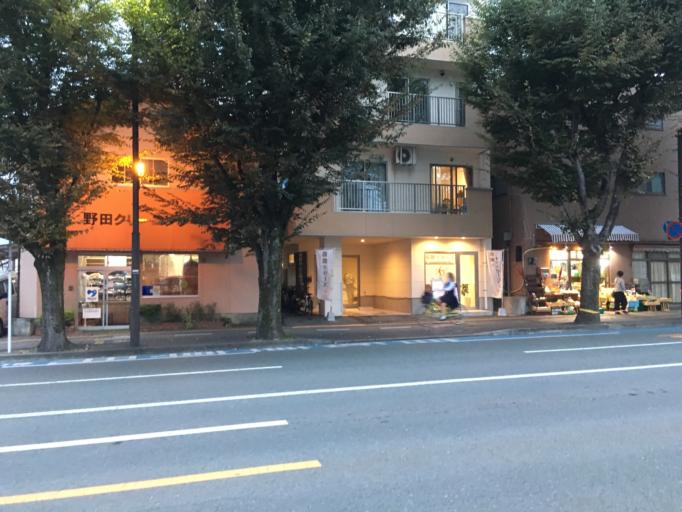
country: JP
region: Kumamoto
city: Kumamoto
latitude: 32.7976
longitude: 130.7280
